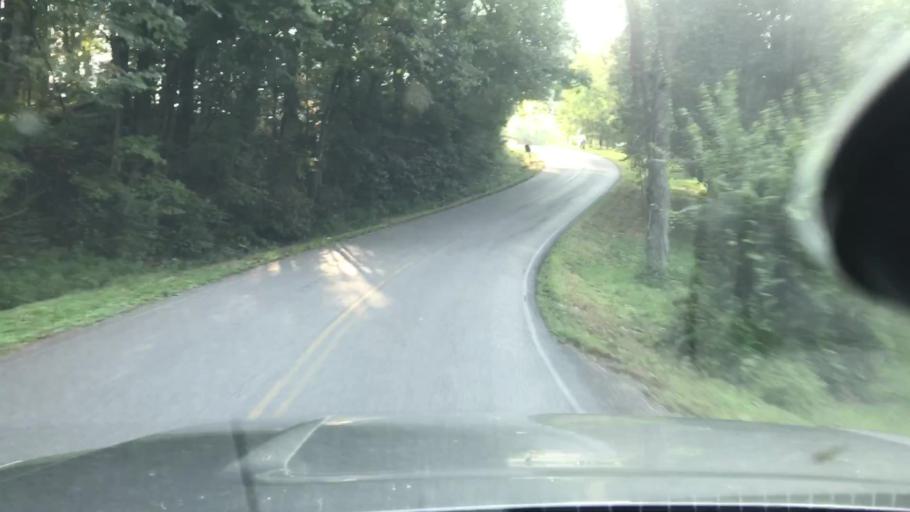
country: US
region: Tennessee
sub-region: Sumner County
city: Gallatin
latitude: 36.4805
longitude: -86.4666
